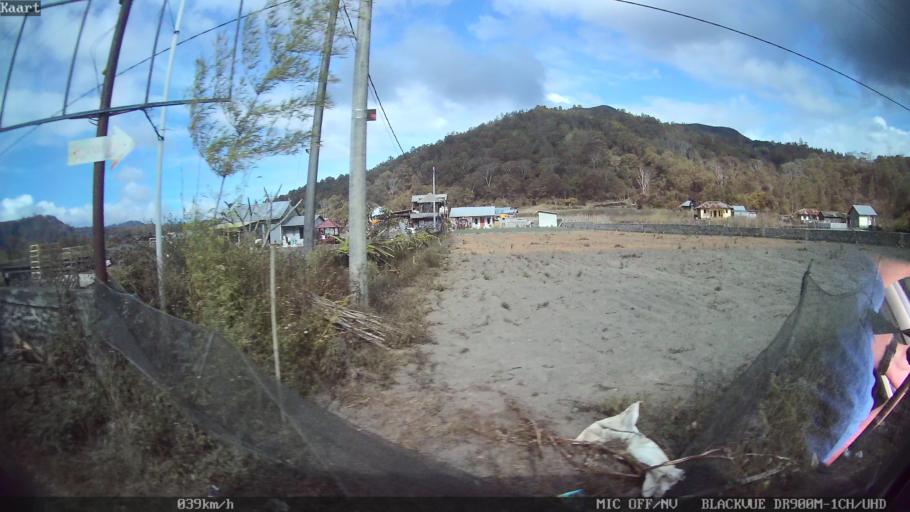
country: ID
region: Bali
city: Banjar Kedisan
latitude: -8.2264
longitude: 115.3592
